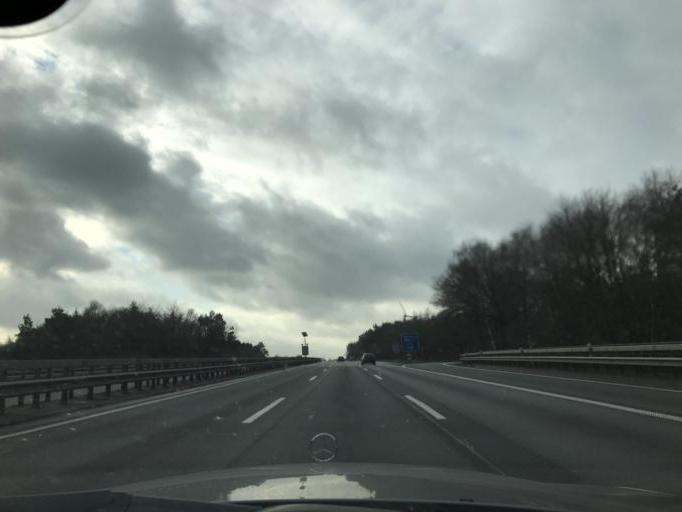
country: DE
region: Lower Saxony
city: Buehren
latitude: 52.8562
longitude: 8.2301
